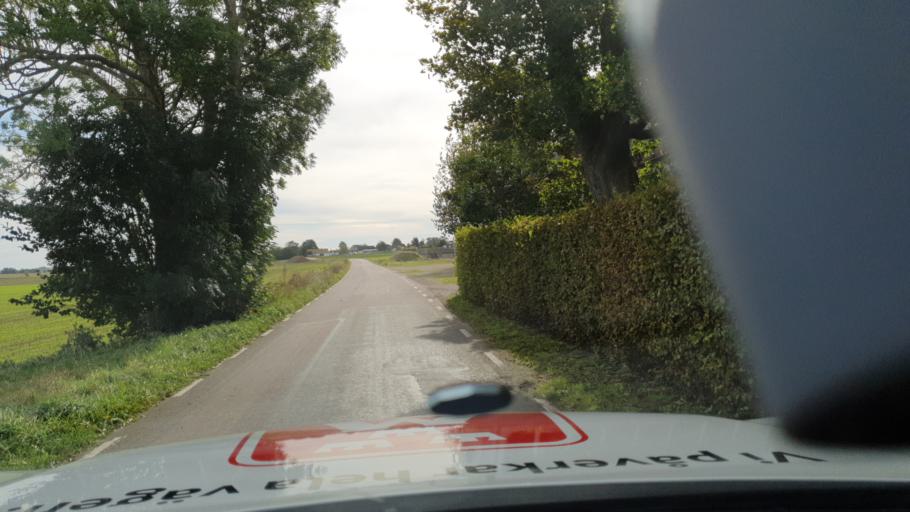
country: SE
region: Skane
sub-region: Vellinge Kommun
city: Vellinge
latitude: 55.4889
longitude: 13.0397
